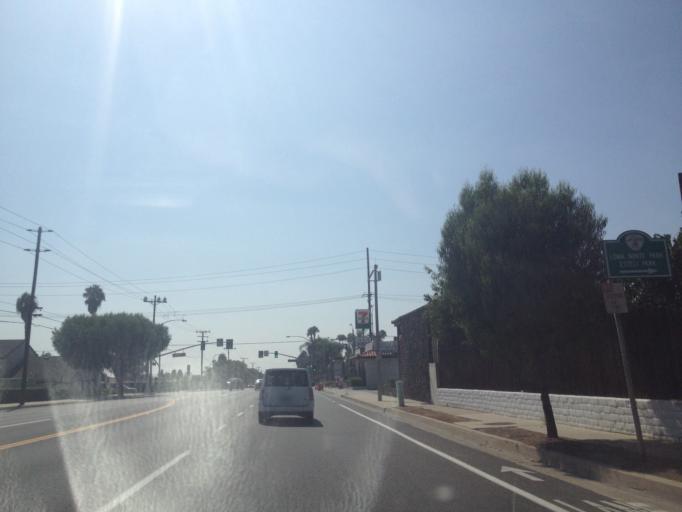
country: US
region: California
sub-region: Orange County
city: La Habra
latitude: 33.9320
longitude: -117.9231
